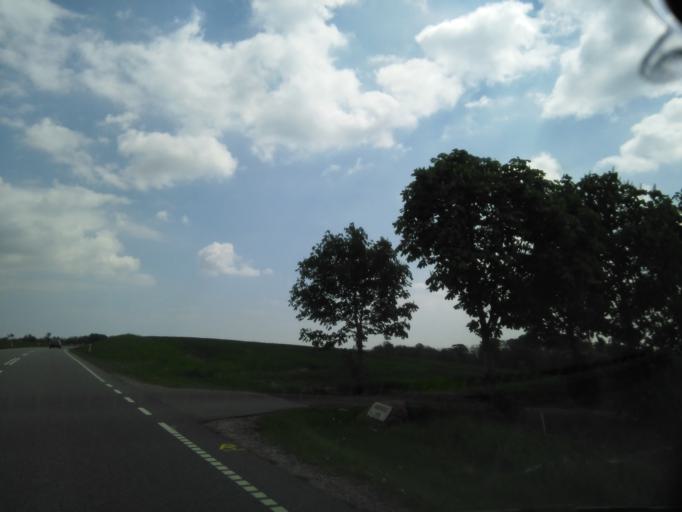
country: DK
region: Central Jutland
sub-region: Skanderborg Kommune
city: Stilling
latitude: 56.0004
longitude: 10.0061
